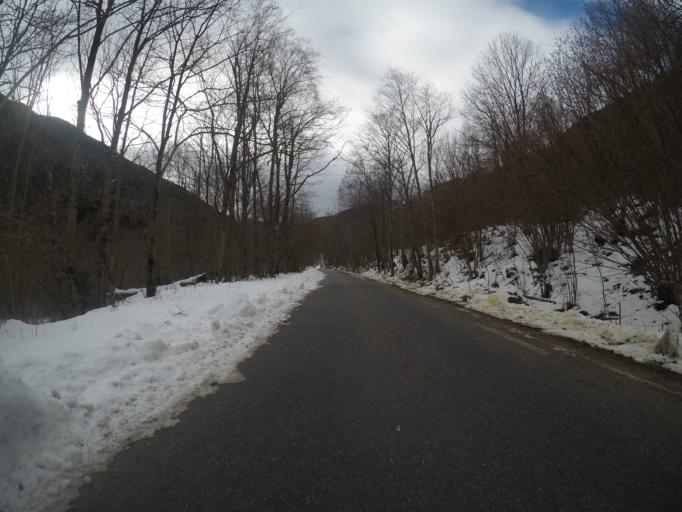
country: BG
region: Kyustendil
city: Sapareva Banya
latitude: 42.1436
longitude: 23.3589
